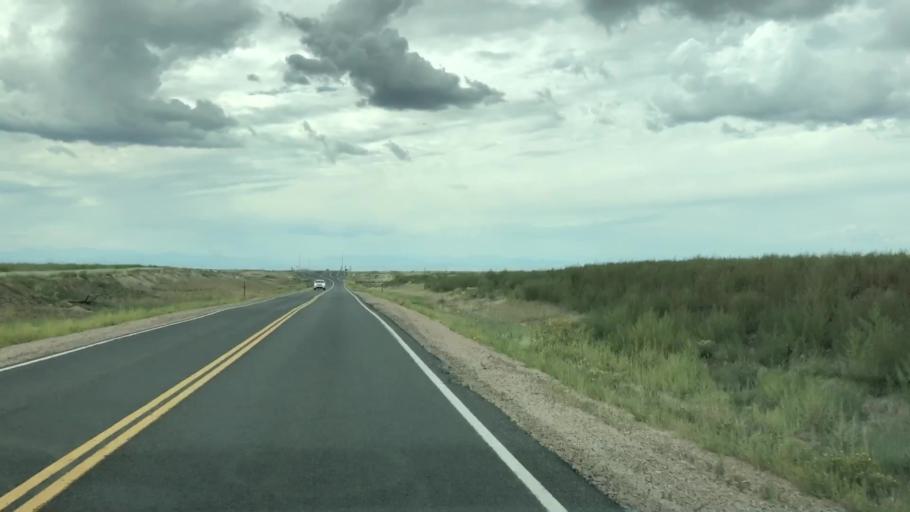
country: US
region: Colorado
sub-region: Adams County
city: Aurora
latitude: 39.7983
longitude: -104.7086
